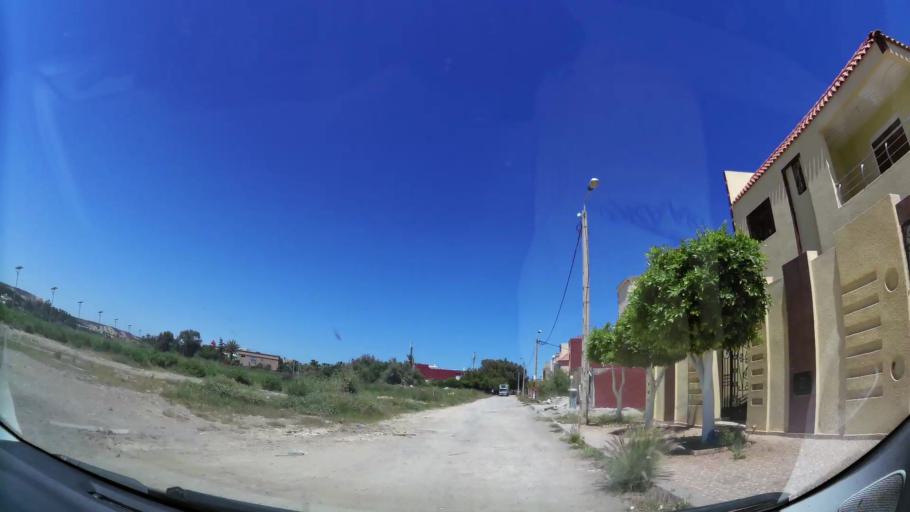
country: MA
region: Oriental
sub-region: Berkane-Taourirt
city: Madagh
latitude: 35.0825
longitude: -2.2437
